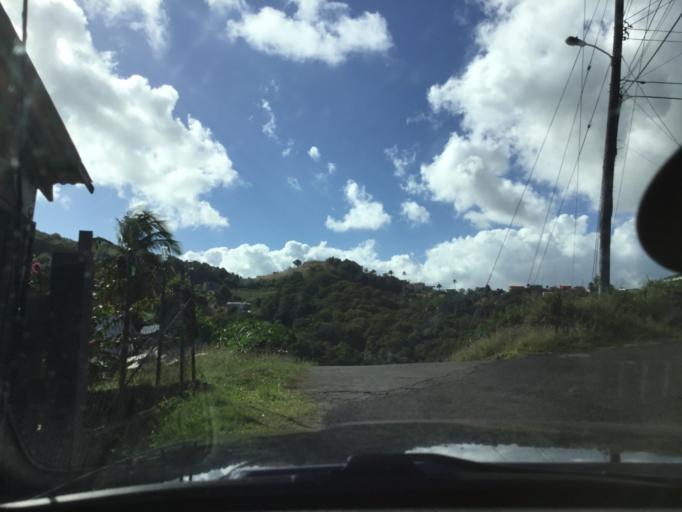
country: VC
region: Saint George
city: Kingstown
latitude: 13.1471
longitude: -61.1790
